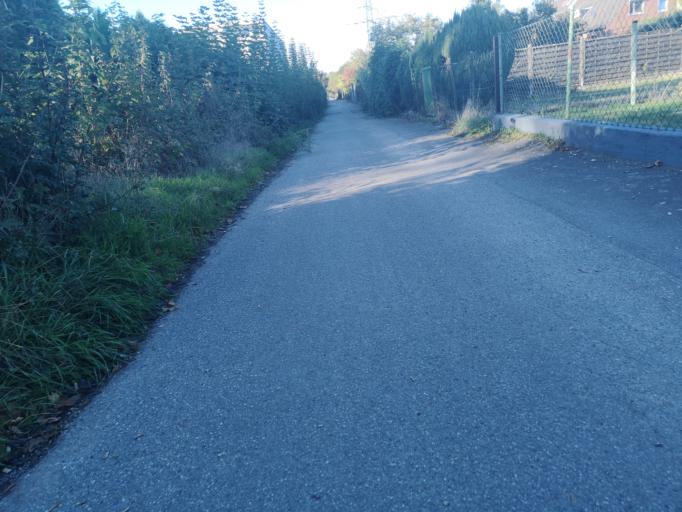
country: DE
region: North Rhine-Westphalia
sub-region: Regierungsbezirk Koln
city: Kreuzau
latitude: 50.7562
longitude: 6.4865
